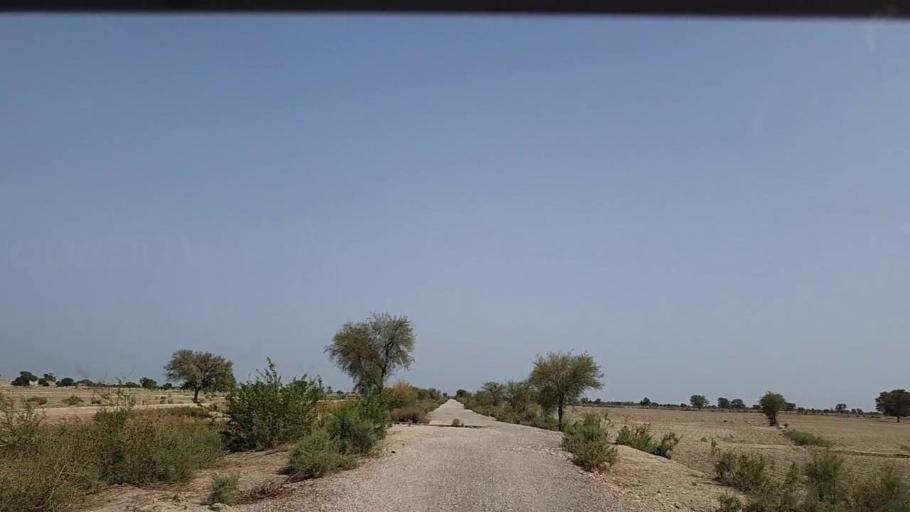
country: PK
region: Sindh
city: Johi
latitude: 26.7537
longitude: 67.6689
